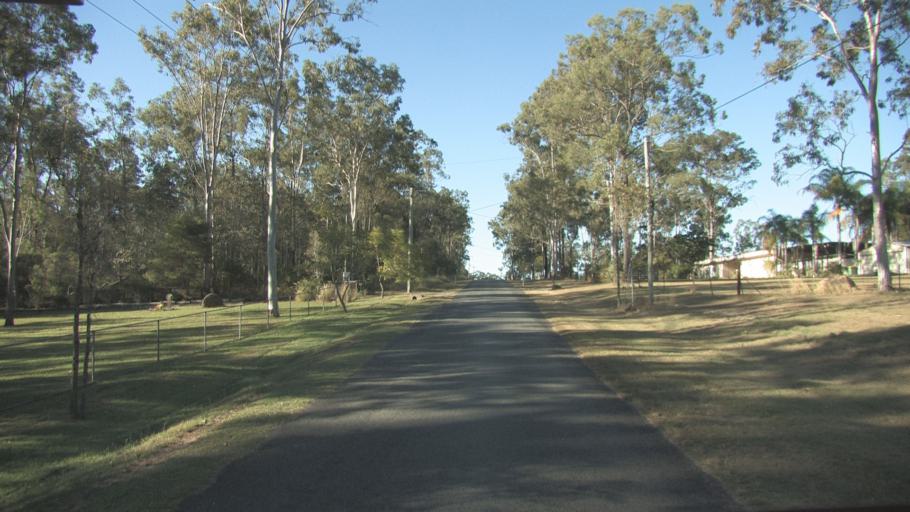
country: AU
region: Queensland
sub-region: Logan
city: North Maclean
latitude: -27.8123
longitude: 153.0470
